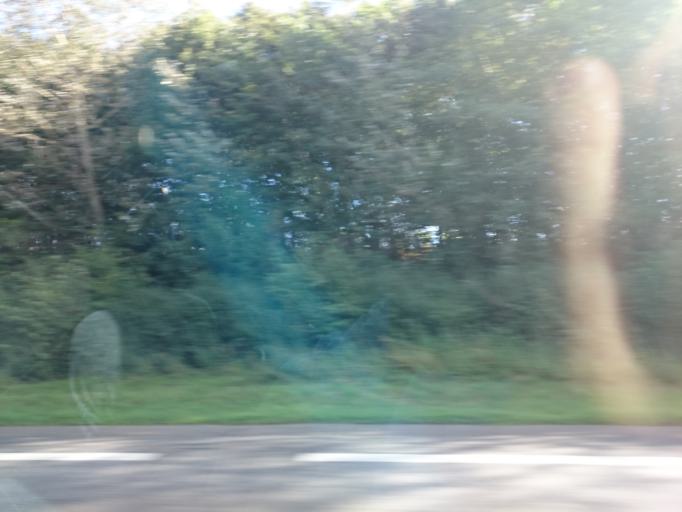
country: DK
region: Central Jutland
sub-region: Horsens Kommune
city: Horsens
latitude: 55.9547
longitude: 9.8360
